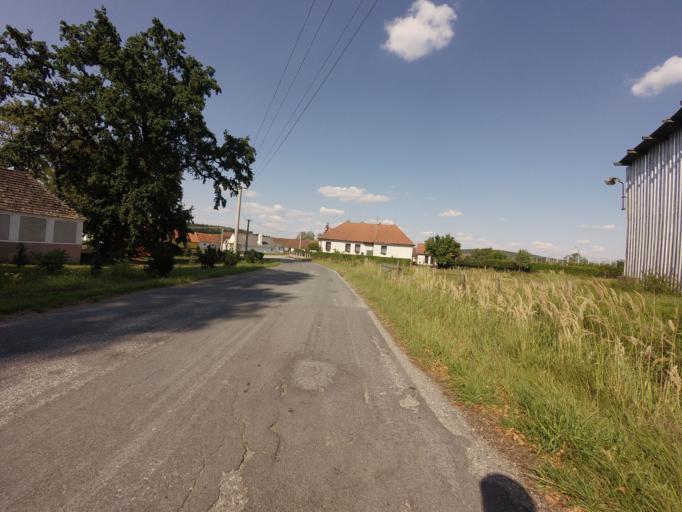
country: CZ
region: Jihocesky
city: Tyn nad Vltavou
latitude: 49.1485
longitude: 14.4449
